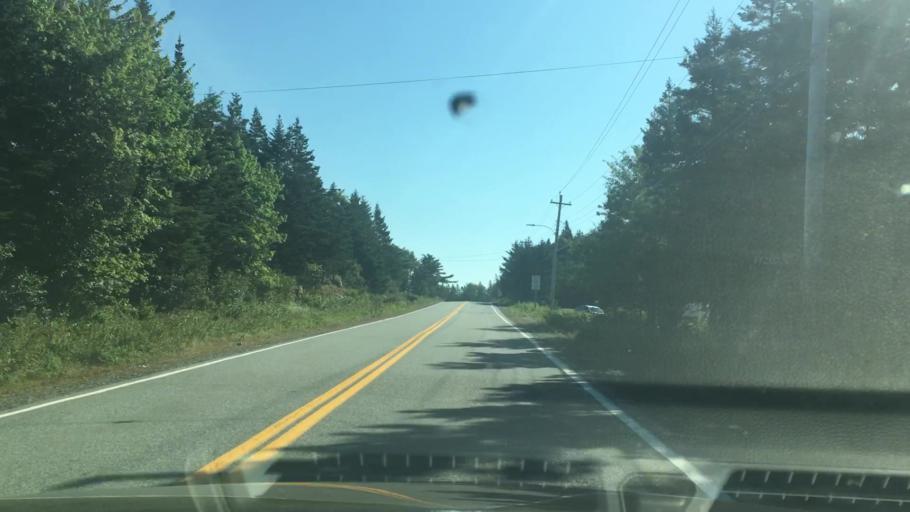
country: CA
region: Nova Scotia
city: New Glasgow
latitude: 44.8037
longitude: -62.7024
